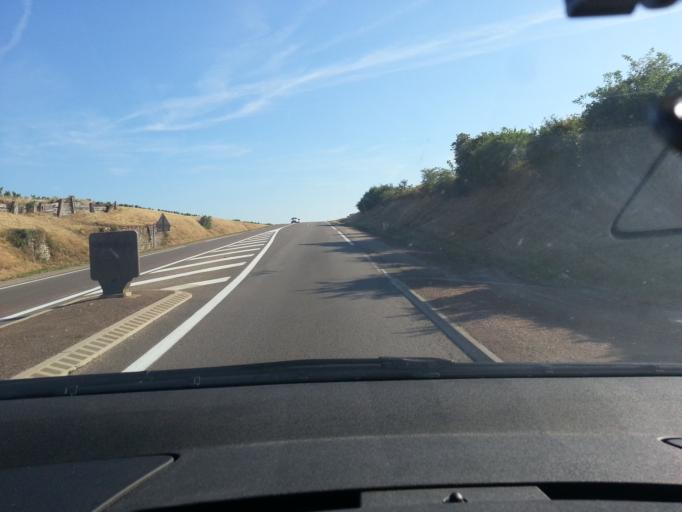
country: FR
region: Bourgogne
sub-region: Departement de la Cote-d'Or
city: Nuits-Saint-Georges
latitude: 47.1533
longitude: 4.9581
